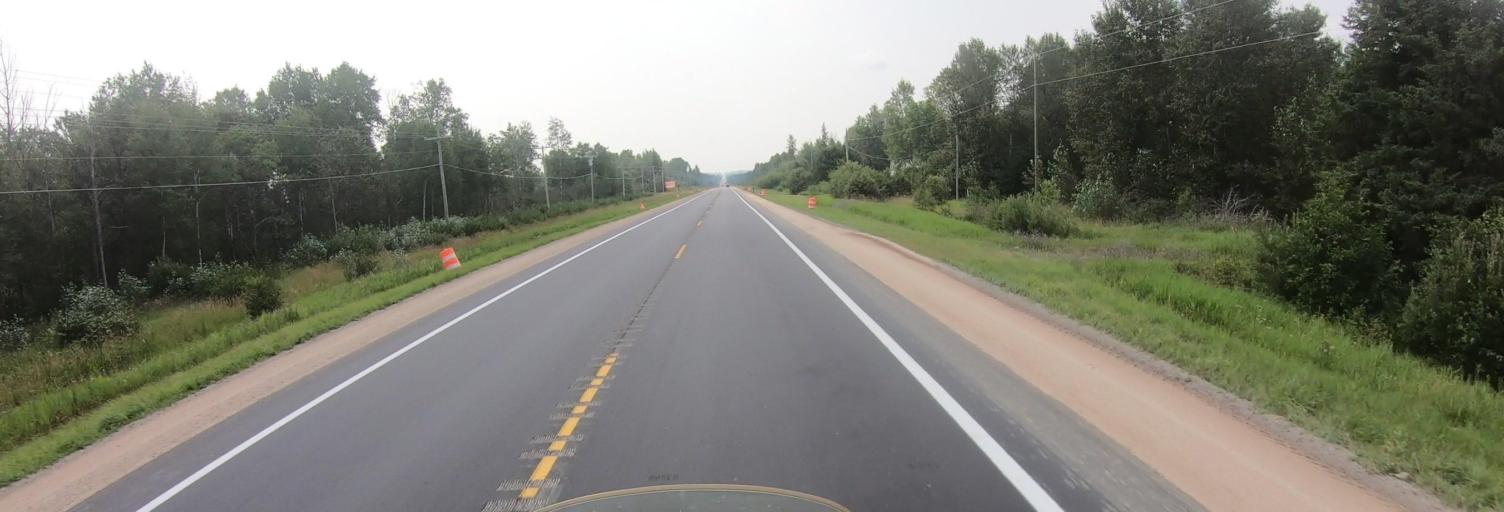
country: US
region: Michigan
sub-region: Luce County
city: Newberry
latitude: 46.3892
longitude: -85.5099
